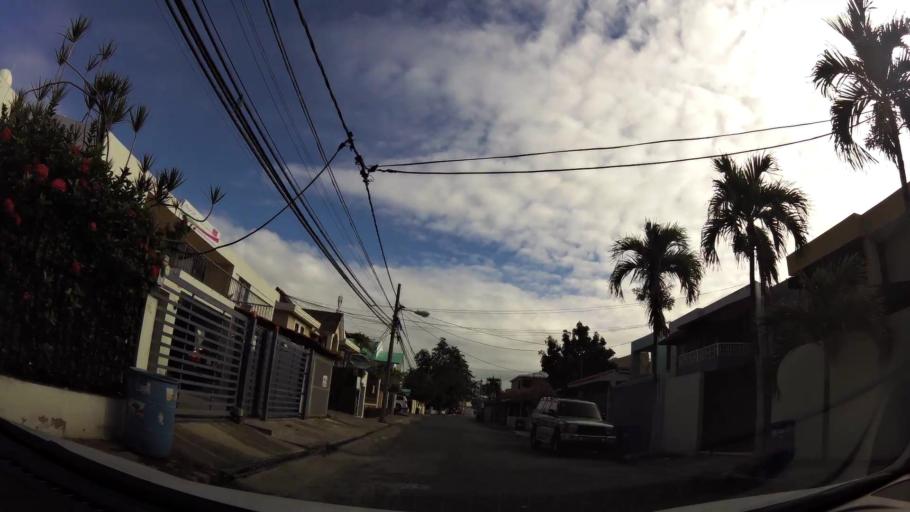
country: DO
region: Nacional
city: La Julia
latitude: 18.4762
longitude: -69.9482
